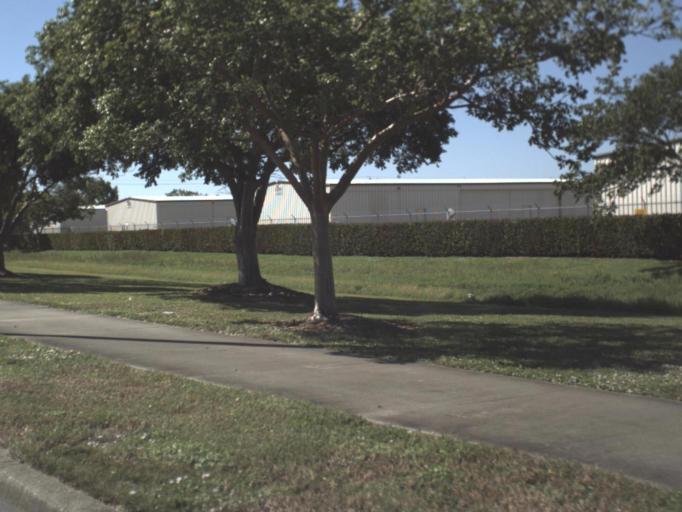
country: US
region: Florida
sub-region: Collier County
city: Naples
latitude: 26.1549
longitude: -81.7670
